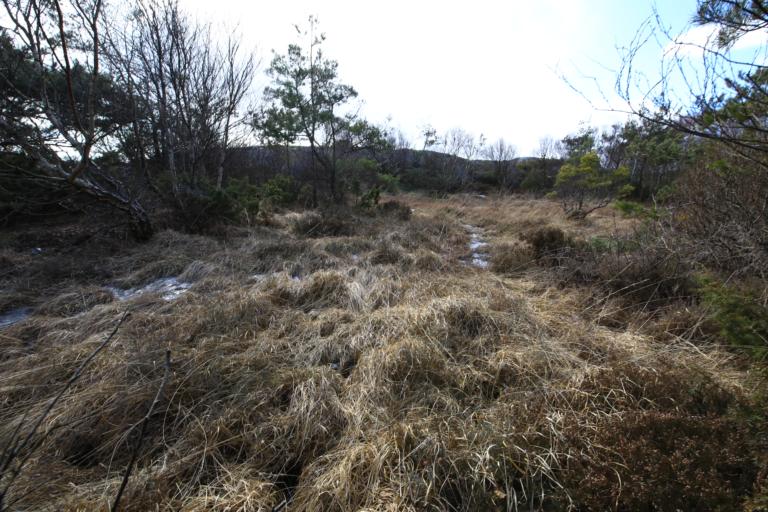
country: SE
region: Halland
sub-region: Kungsbacka Kommun
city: Frillesas
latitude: 57.2139
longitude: 12.1435
